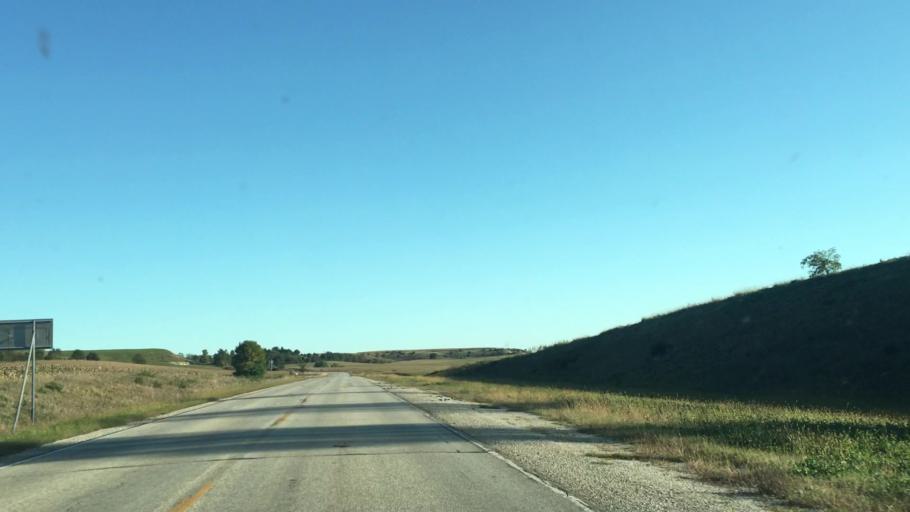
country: US
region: Minnesota
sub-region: Fillmore County
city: Chatfield
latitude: 43.8521
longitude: -92.1083
